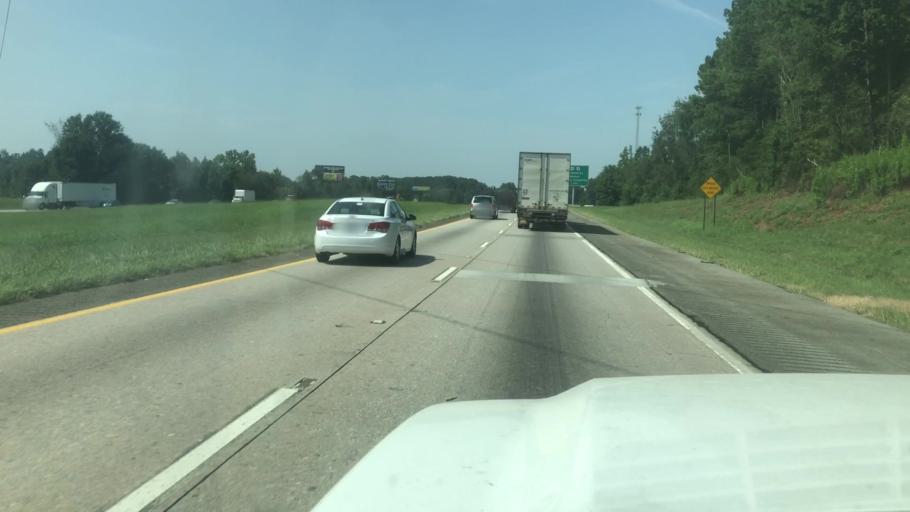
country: US
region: Georgia
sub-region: Jackson County
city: Commerce
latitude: 34.2667
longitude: -83.4458
